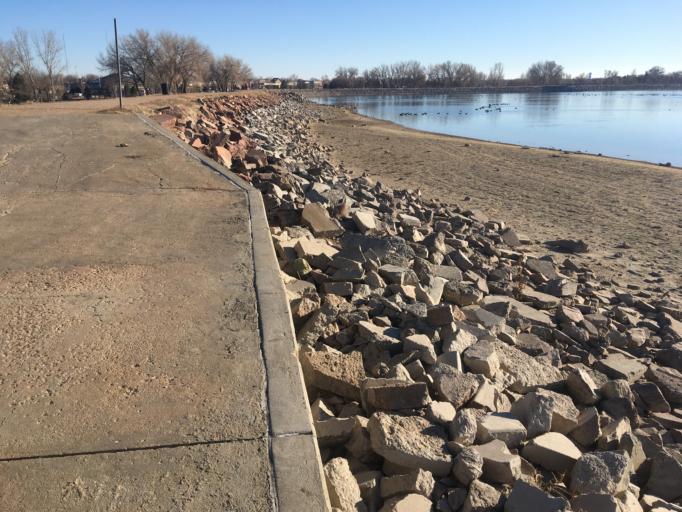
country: US
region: Colorado
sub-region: Weld County
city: Firestone
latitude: 40.1236
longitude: -104.9447
